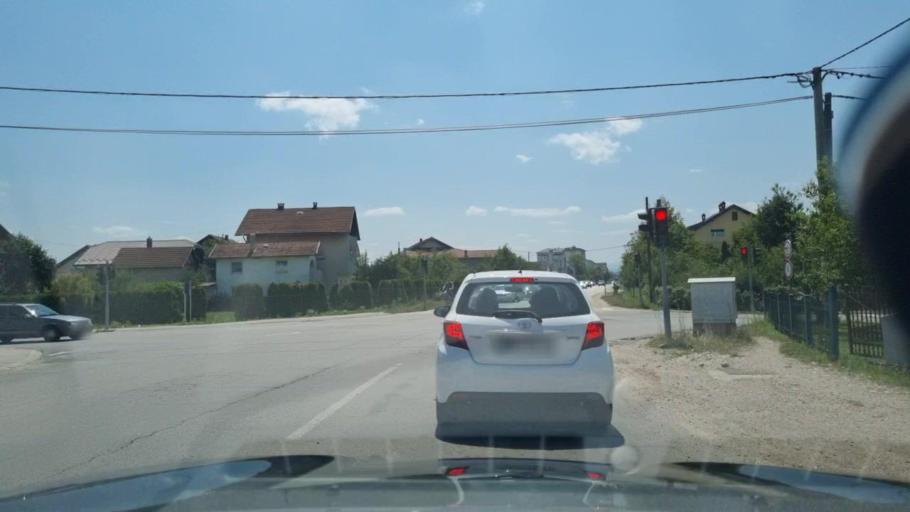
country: BA
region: Federation of Bosnia and Herzegovina
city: Sanski Most
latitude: 44.7686
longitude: 16.6709
